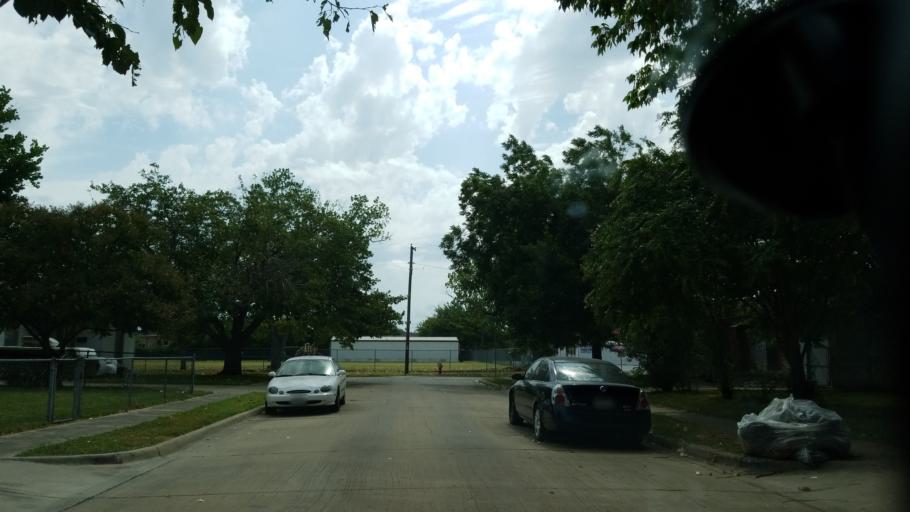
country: US
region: Texas
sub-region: Dallas County
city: Grand Prairie
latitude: 32.7512
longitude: -96.9818
